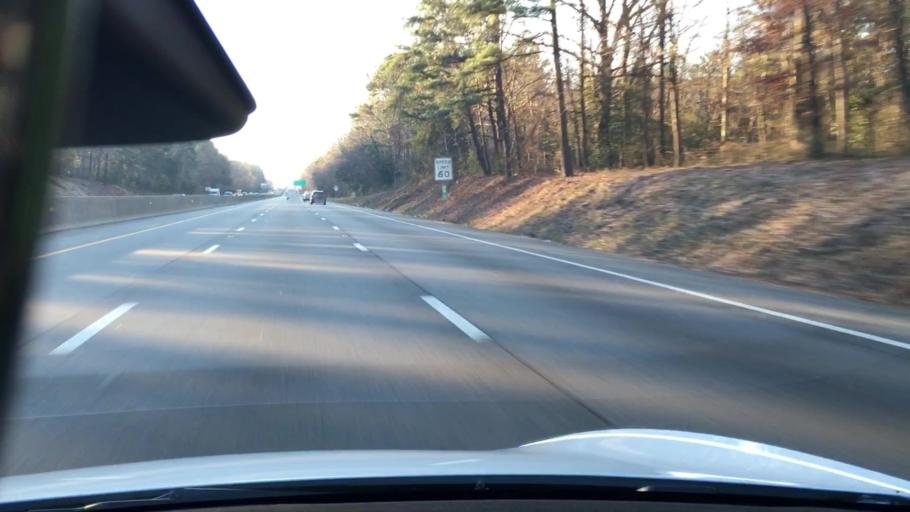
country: US
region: Virginia
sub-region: Chesterfield County
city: Bon Air
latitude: 37.4948
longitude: -77.5222
